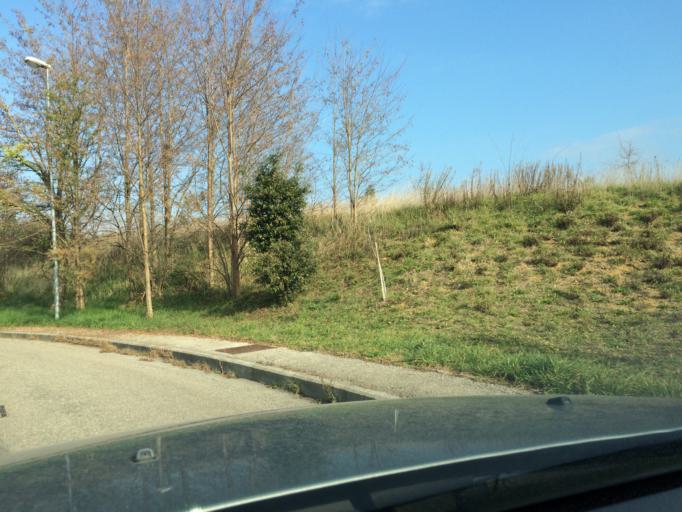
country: IT
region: Umbria
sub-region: Provincia di Perugia
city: Via Lippia
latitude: 43.1004
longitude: 12.4927
